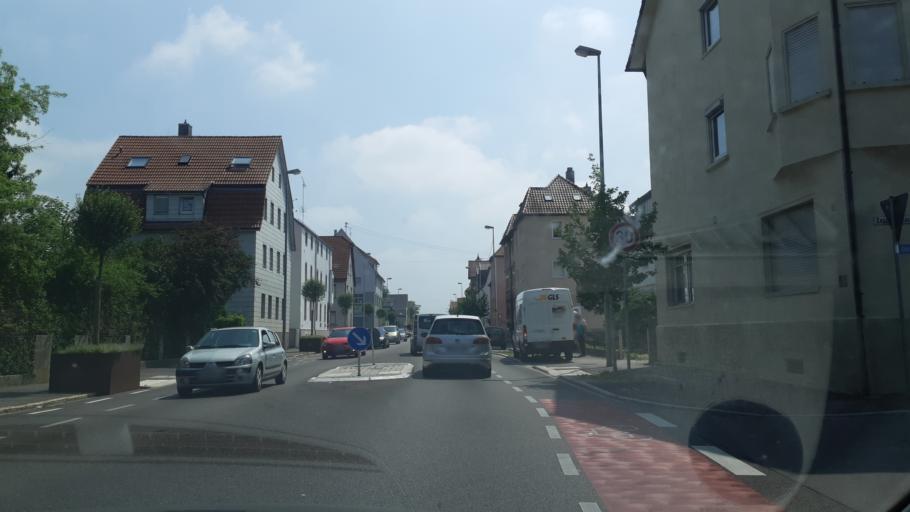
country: DE
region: Baden-Wuerttemberg
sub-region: Regierungsbezirk Stuttgart
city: Eislingen
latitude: 48.6958
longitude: 9.6956
